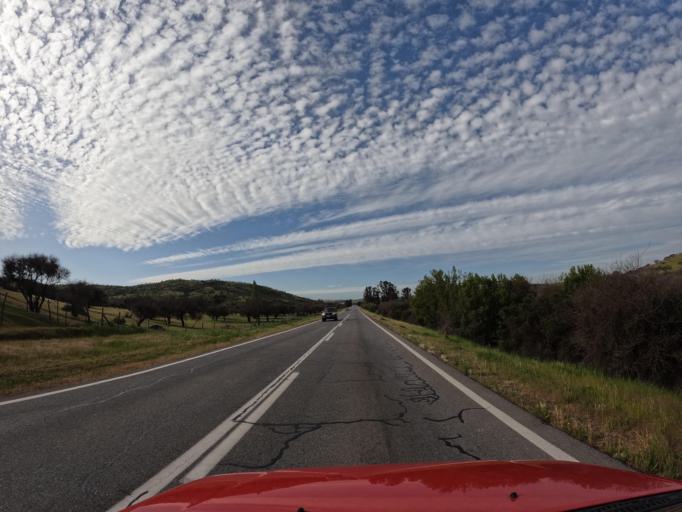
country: CL
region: O'Higgins
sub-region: Provincia de Colchagua
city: Santa Cruz
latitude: -34.2955
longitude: -71.7315
